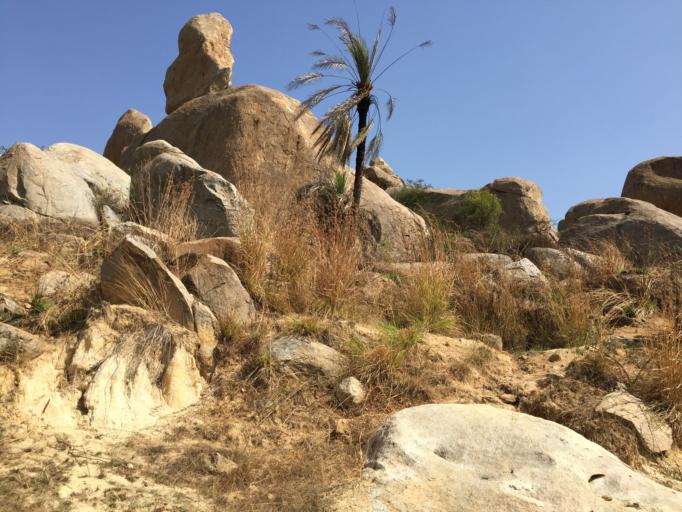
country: IN
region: Karnataka
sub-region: Kolar
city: Kolar
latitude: 13.1368
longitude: 78.0132
